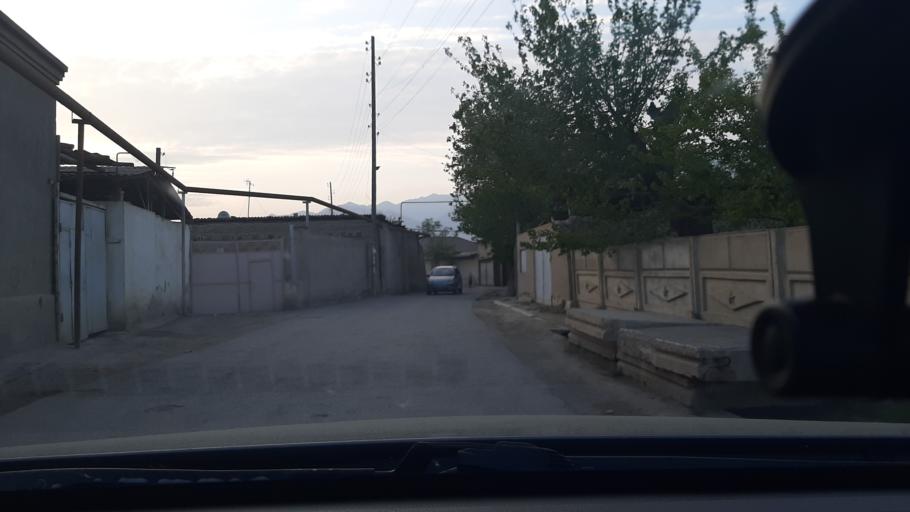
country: TJ
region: Viloyati Sughd
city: Khujand
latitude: 40.2942
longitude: 69.6553
